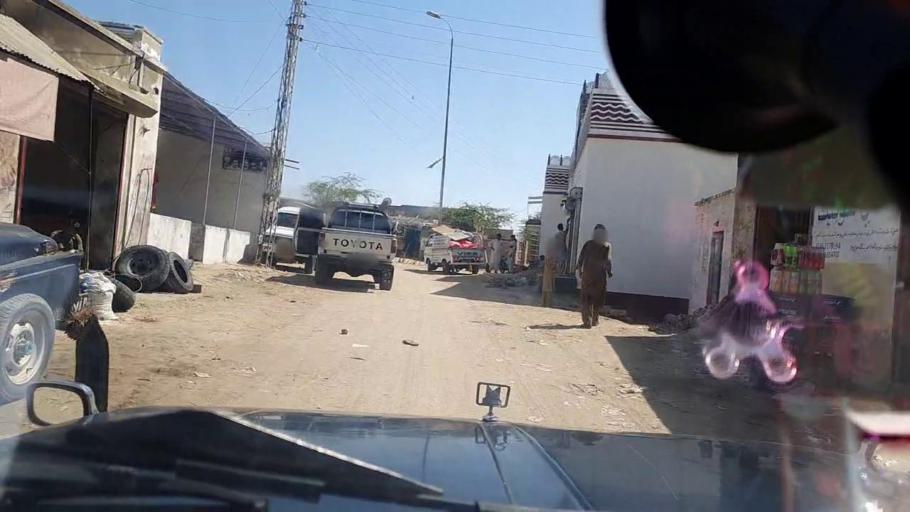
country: PK
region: Sindh
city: Diplo
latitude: 24.4652
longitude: 69.5835
